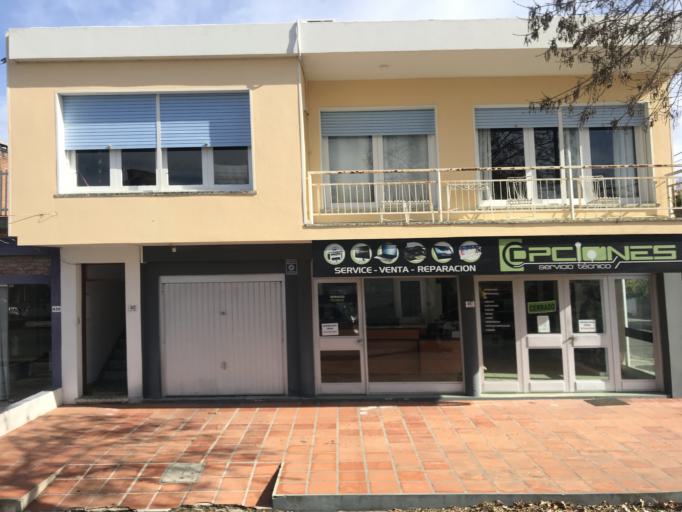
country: UY
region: Colonia
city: Colonia del Sacramento
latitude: -34.4657
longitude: -57.8385
